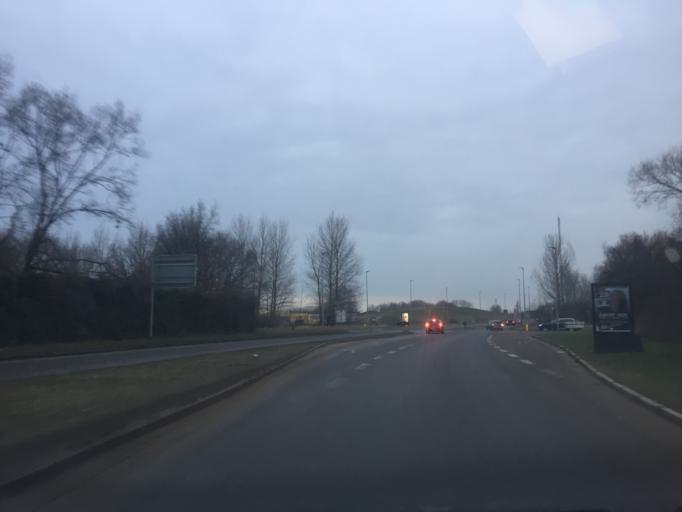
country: DK
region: Zealand
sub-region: Koge Kommune
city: Koge
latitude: 55.4691
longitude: 12.1882
